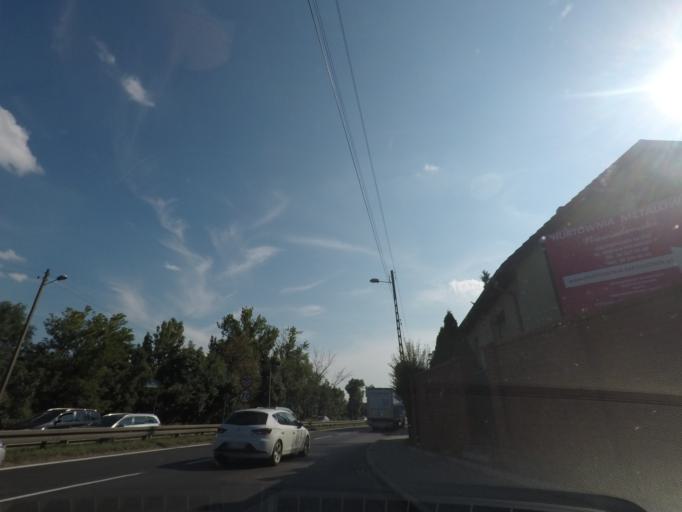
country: PL
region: Silesian Voivodeship
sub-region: Powiat czestochowski
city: Huta Stara B
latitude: 50.7573
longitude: 19.1573
